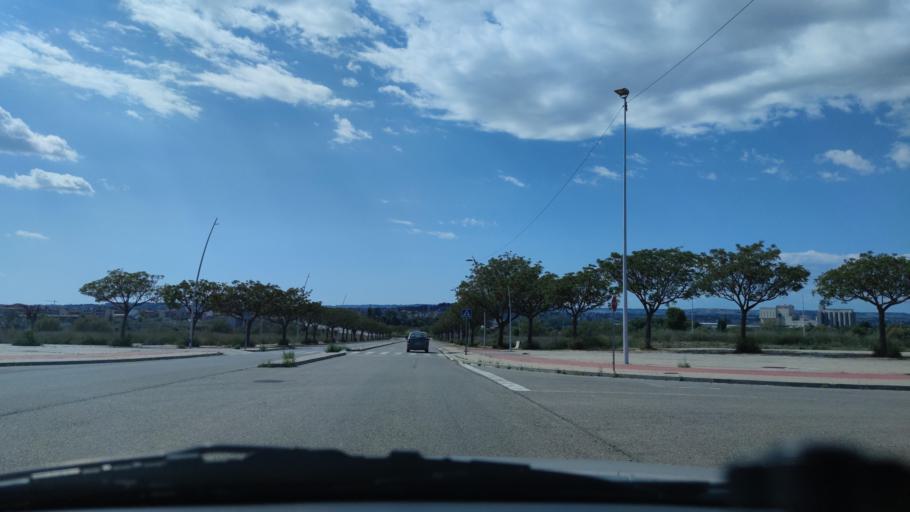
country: ES
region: Catalonia
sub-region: Provincia de Lleida
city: Lleida
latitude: 41.6061
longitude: 0.6572
